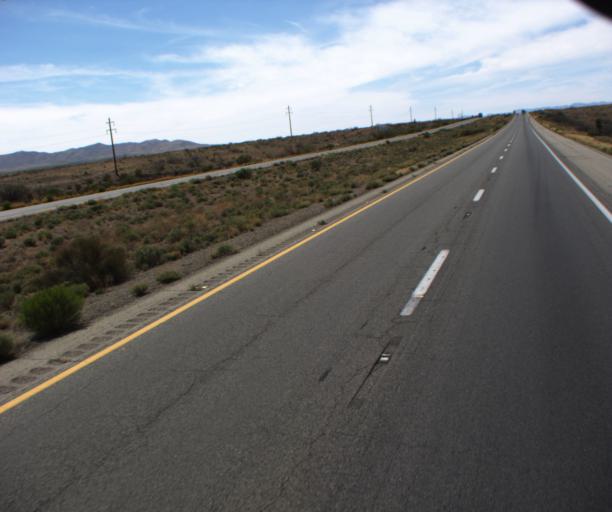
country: US
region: Arizona
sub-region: Cochise County
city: Willcox
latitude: 32.3628
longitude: -109.6402
